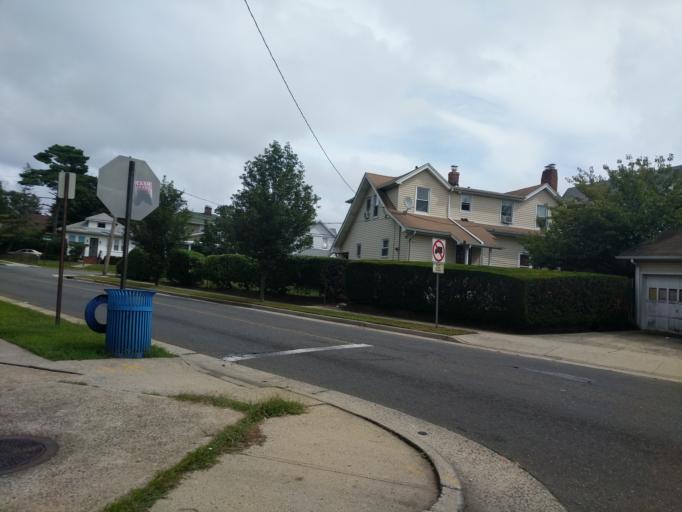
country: US
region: New York
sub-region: Nassau County
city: Hempstead
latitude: 40.7122
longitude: -73.6160
